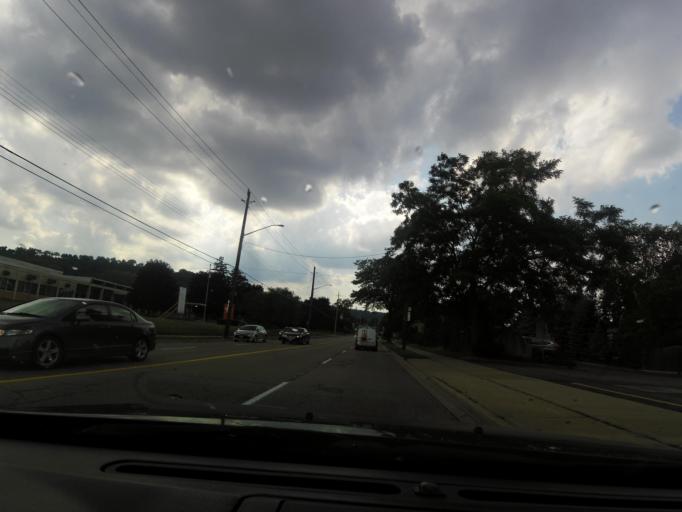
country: CA
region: Ontario
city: Hamilton
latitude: 43.2318
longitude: -79.8082
